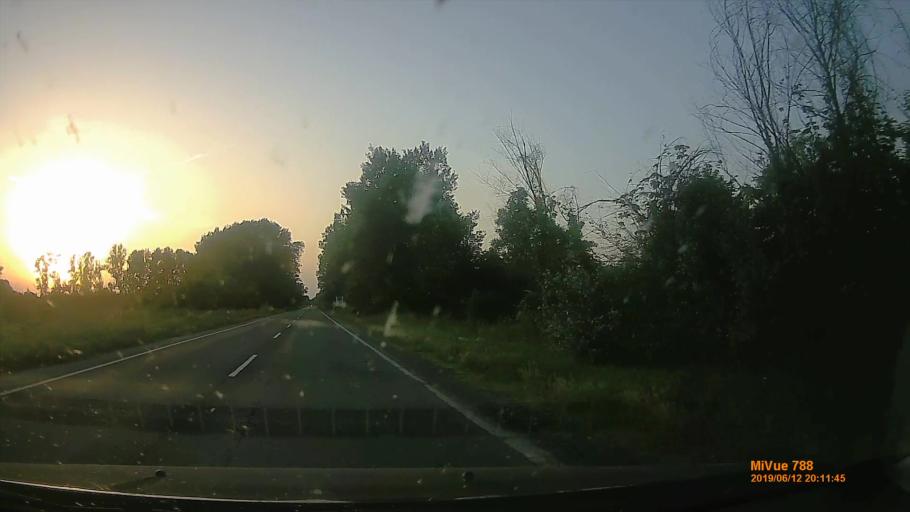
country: HU
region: Pest
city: Ocsa
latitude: 47.2796
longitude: 19.1997
